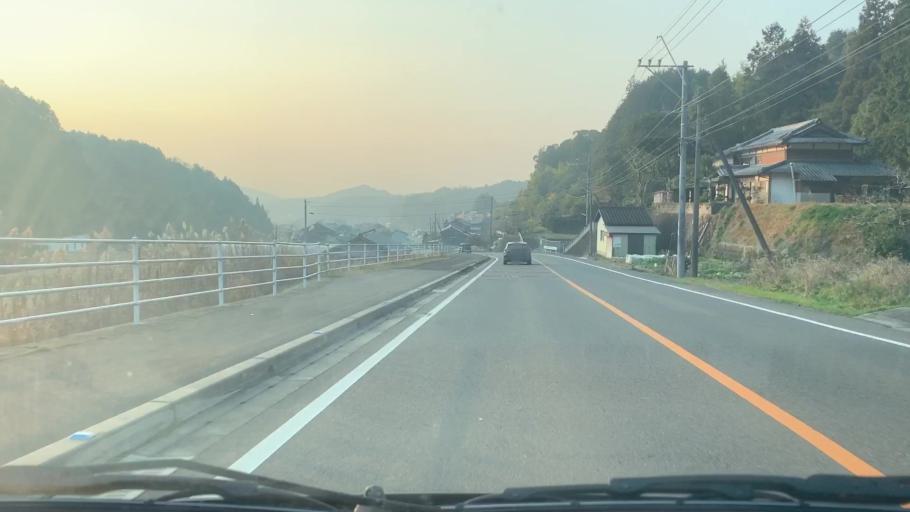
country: JP
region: Saga Prefecture
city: Takeocho-takeo
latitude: 33.2554
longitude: 130.0140
